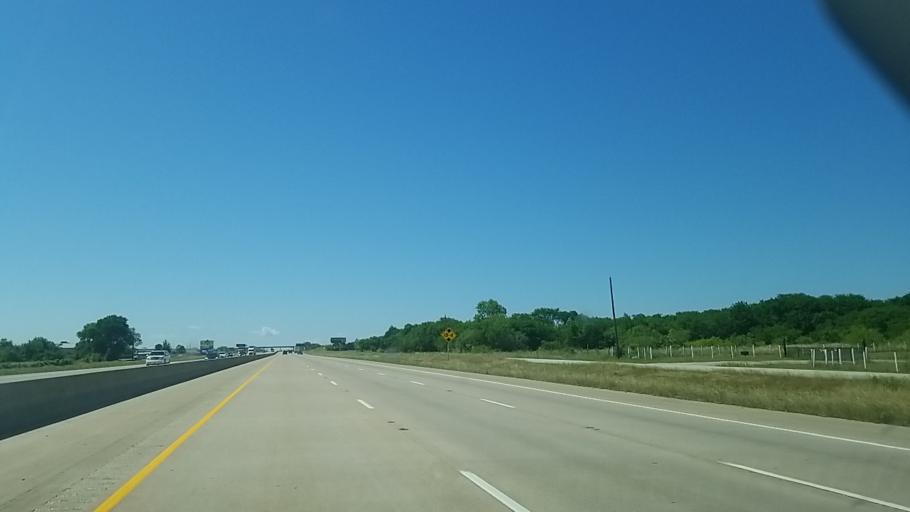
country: US
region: Texas
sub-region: Navarro County
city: Corsicana
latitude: 32.2087
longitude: -96.4784
